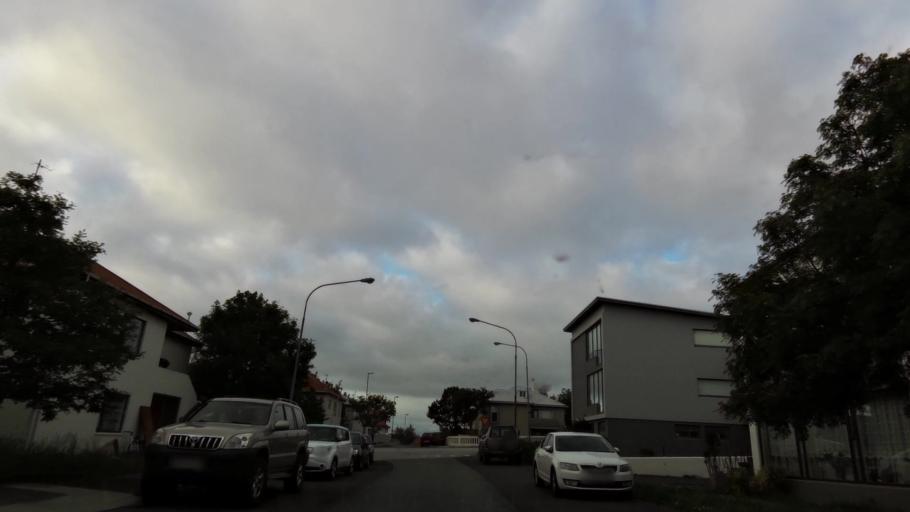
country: IS
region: Capital Region
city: Hafnarfjoerdur
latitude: 64.0636
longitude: -21.9478
